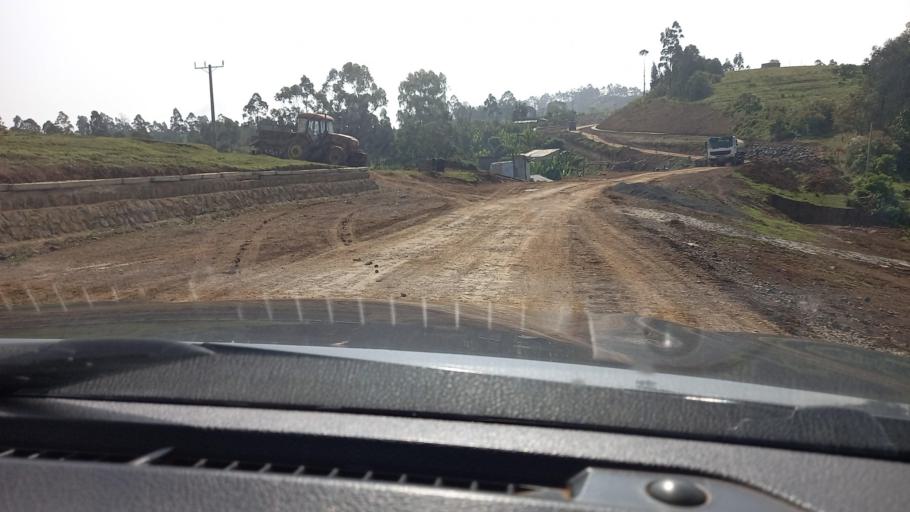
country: ET
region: Southern Nations, Nationalities, and People's Region
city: Mizan Teferi
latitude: 6.1657
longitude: 35.5882
